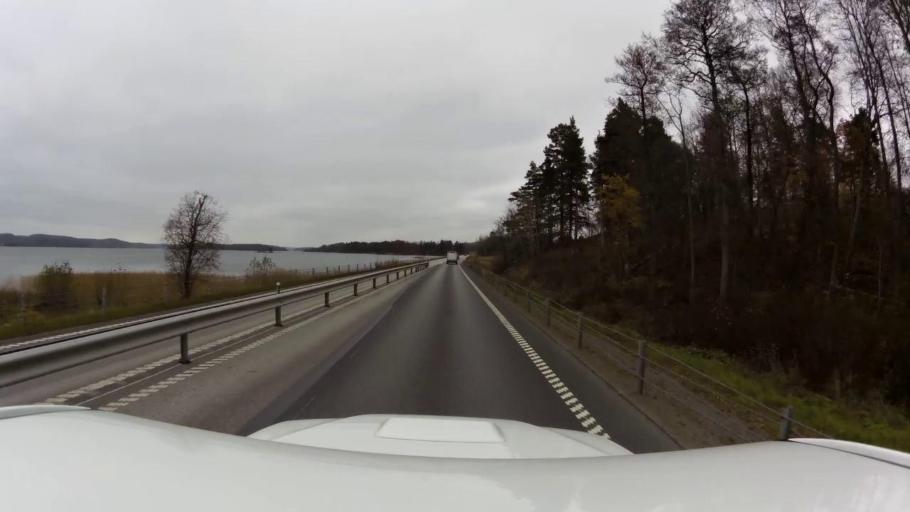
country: SE
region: OEstergoetland
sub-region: Kinda Kommun
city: Rimforsa
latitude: 58.1506
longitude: 15.6803
